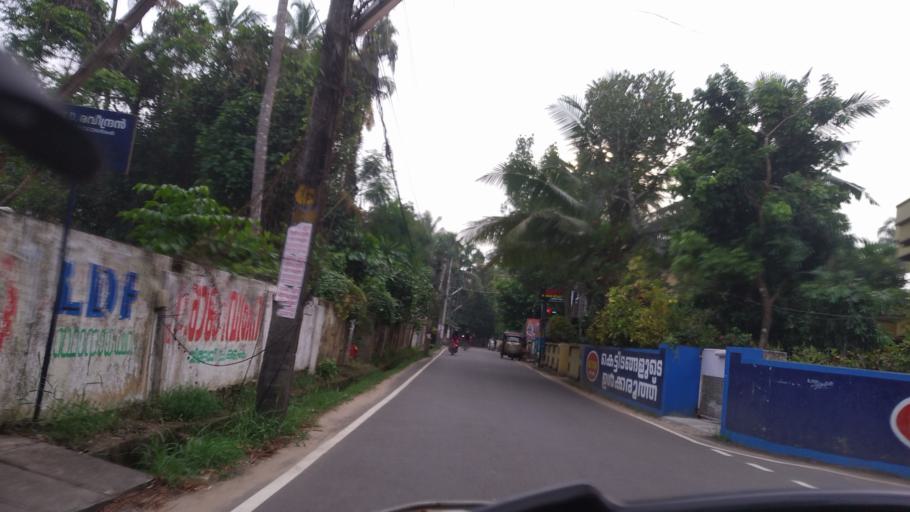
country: IN
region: Kerala
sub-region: Thrissur District
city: Kodungallur
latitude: 10.1390
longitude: 76.2279
